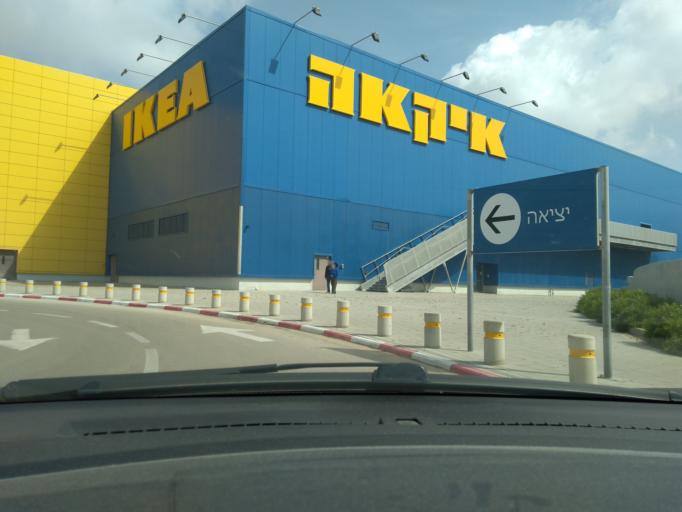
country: IL
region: Central District
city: Even Yehuda
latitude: 32.2731
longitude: 34.8601
